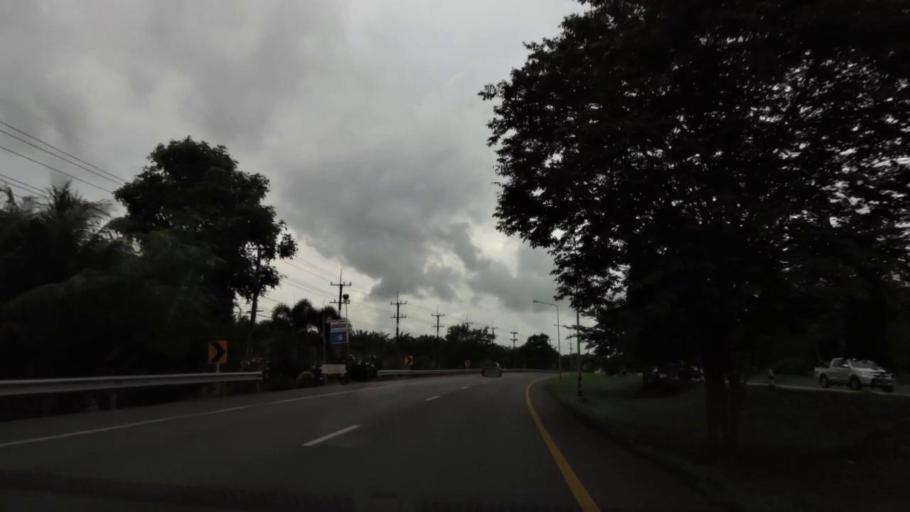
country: TH
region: Chanthaburi
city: Tha Mai
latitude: 12.6992
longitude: 101.9868
